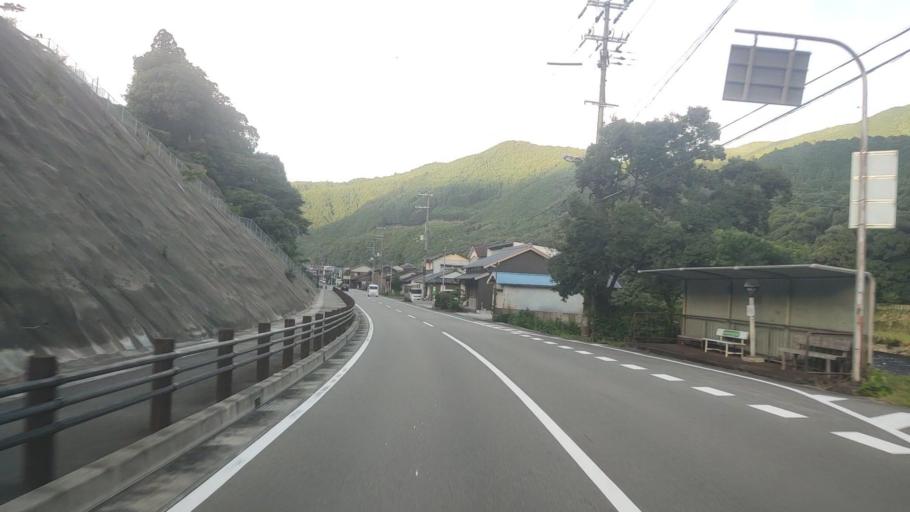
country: JP
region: Wakayama
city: Tanabe
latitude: 33.7877
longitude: 135.5127
